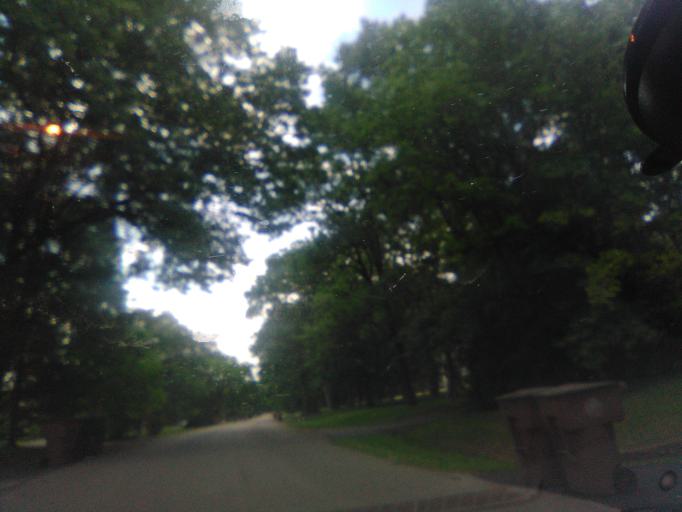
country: US
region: Tennessee
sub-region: Davidson County
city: Belle Meade
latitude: 36.1213
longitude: -86.8760
